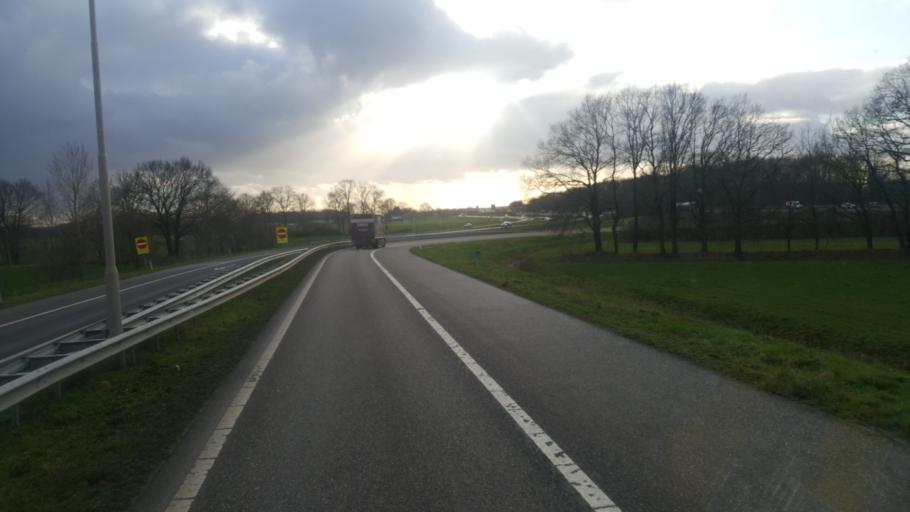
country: NL
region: Limburg
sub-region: Gemeente Venlo
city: Tegelen
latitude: 51.3158
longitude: 6.1365
